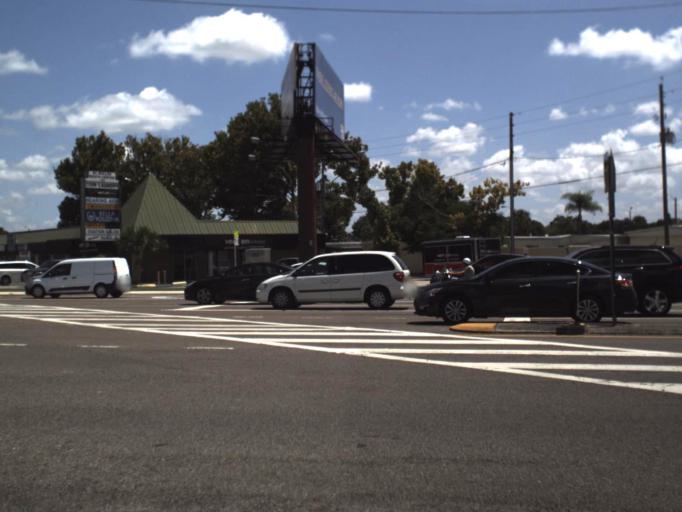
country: US
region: Florida
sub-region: Pinellas County
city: Safety Harbor
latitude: 28.0229
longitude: -82.7092
